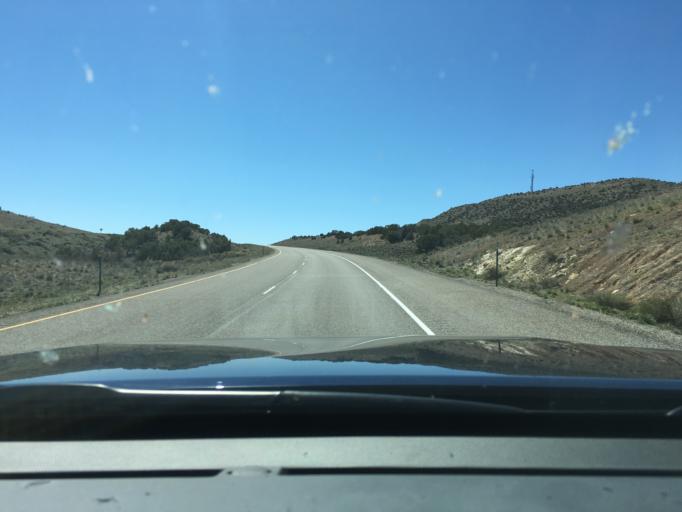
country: US
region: Colorado
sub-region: Mesa County
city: Loma
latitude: 39.2202
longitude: -108.9596
